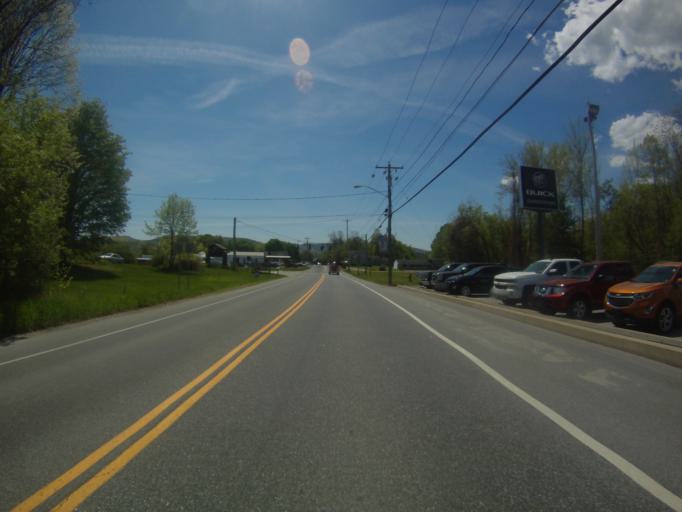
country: US
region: New York
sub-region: Essex County
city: Ticonderoga
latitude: 43.8554
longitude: -73.4382
